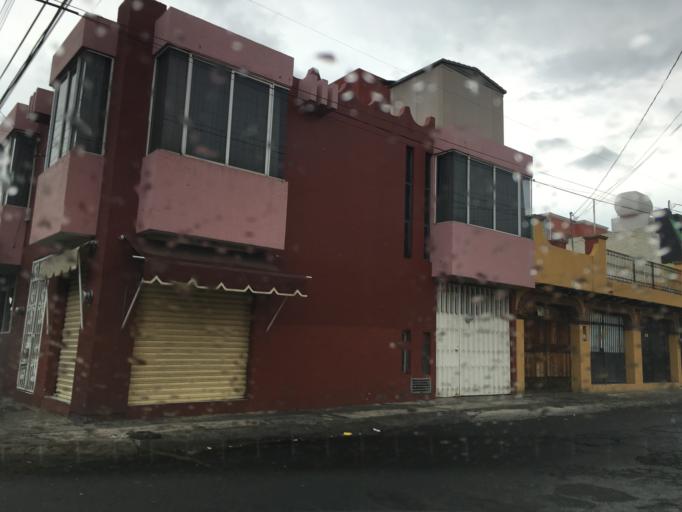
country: MX
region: Michoacan
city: Morelia
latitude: 19.6870
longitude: -101.1697
